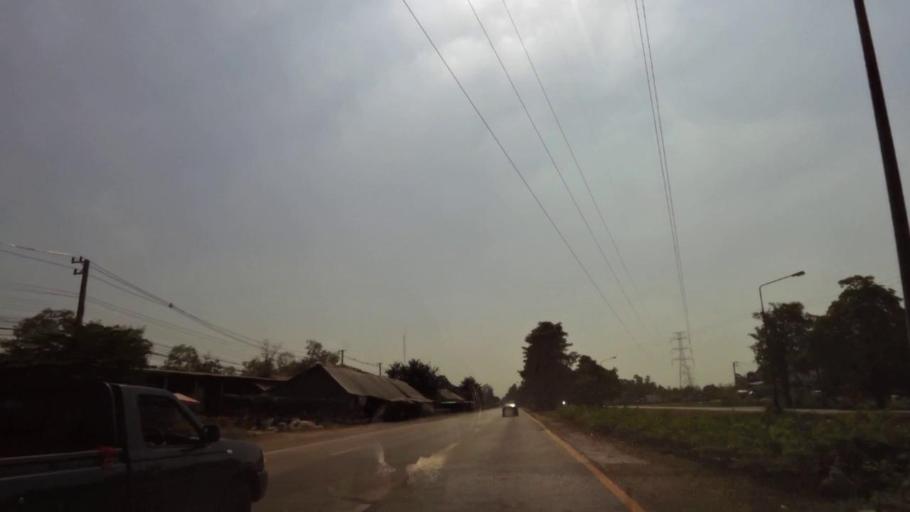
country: TH
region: Phichit
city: Wachira Barami
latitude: 16.5058
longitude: 100.1434
